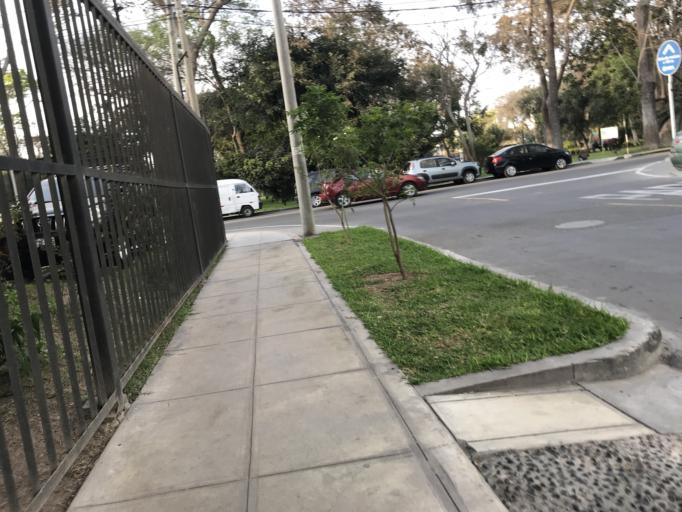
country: PE
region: Lima
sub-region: Lima
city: San Isidro
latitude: -12.0897
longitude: -77.0409
